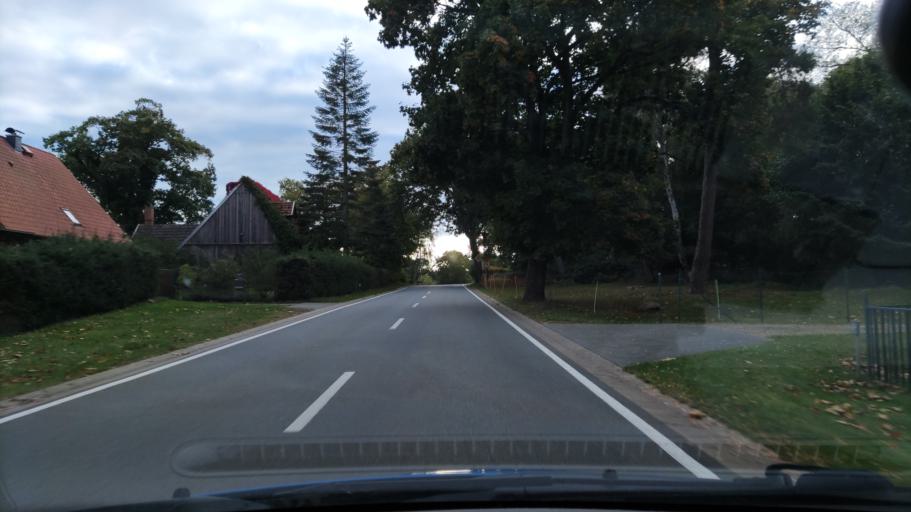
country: DE
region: Schleswig-Holstein
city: Langenlehsten
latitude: 53.4283
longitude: 10.8456
